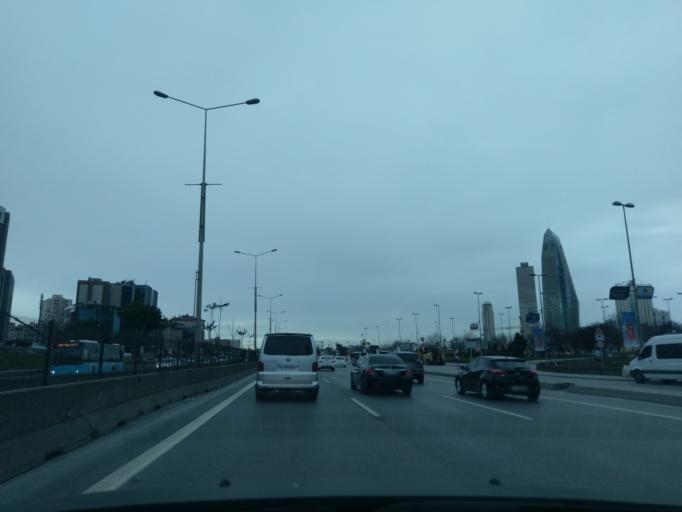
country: TR
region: Istanbul
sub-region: Atasehir
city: Atasehir
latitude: 40.9741
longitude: 29.0998
